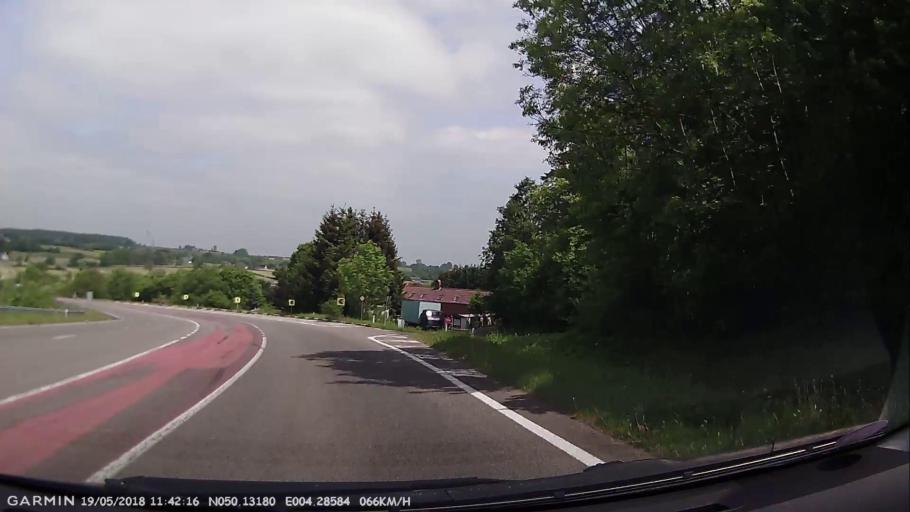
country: BE
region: Wallonia
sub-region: Province du Hainaut
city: Froidchapelle
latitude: 50.1319
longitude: 4.2860
